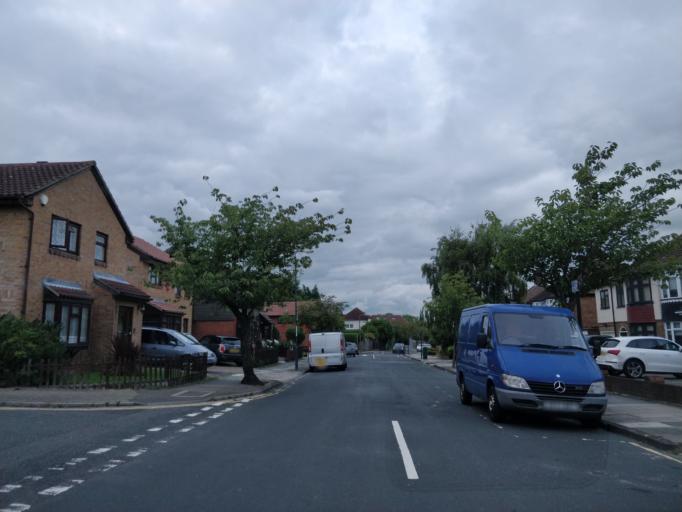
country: GB
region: England
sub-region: Greater London
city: Chislehurst
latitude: 51.4359
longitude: 0.0525
